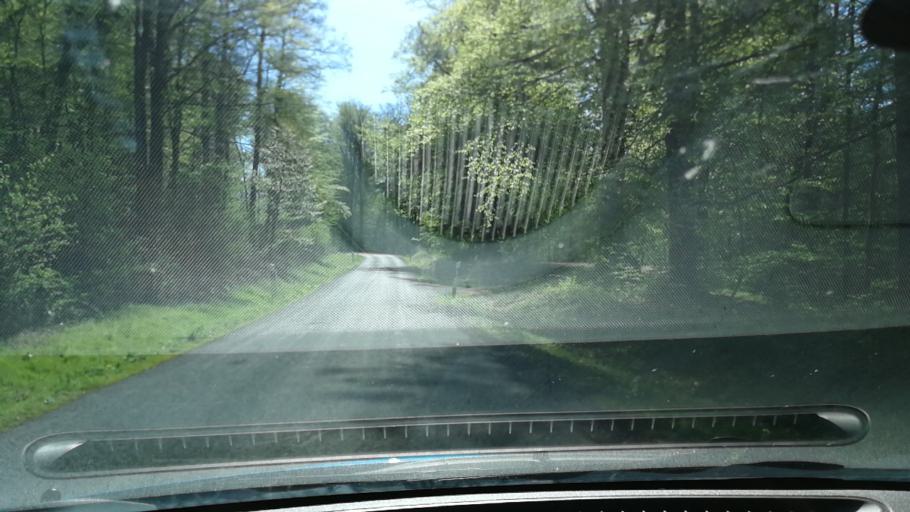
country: DE
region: Lower Saxony
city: Buhren
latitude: 51.5417
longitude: 9.6558
